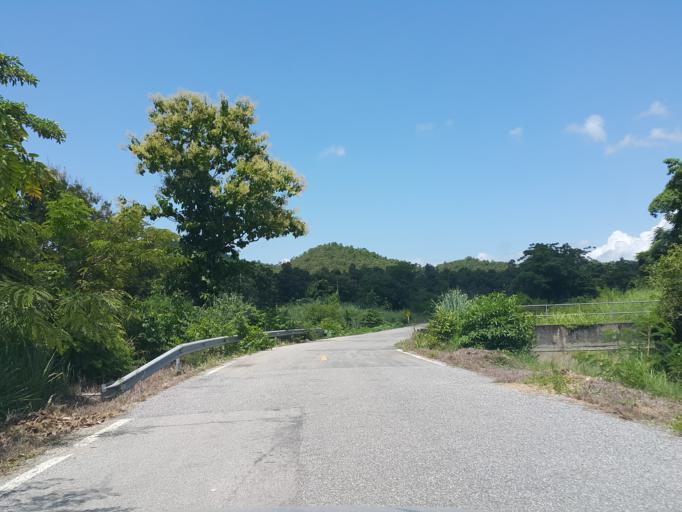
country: TH
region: Chiang Mai
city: San Kamphaeng
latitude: 18.6989
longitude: 99.1786
